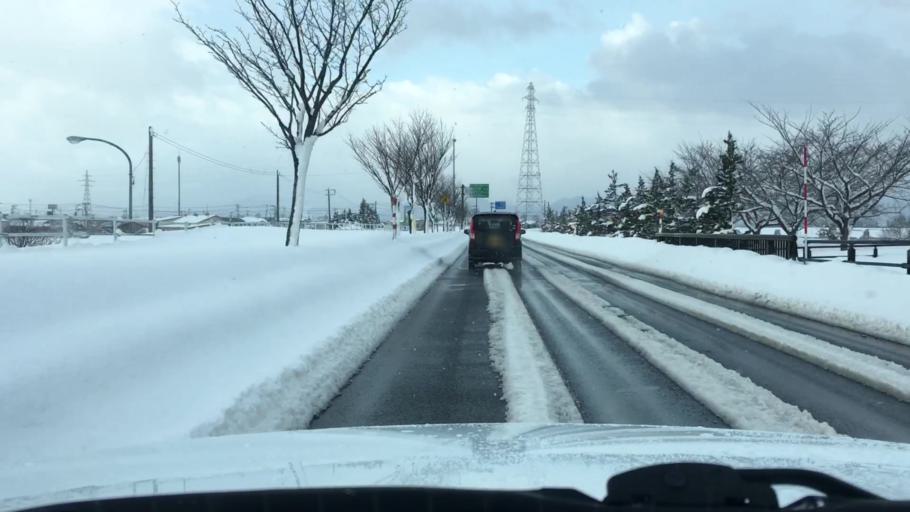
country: JP
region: Aomori
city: Hirosaki
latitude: 40.6305
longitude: 140.4736
